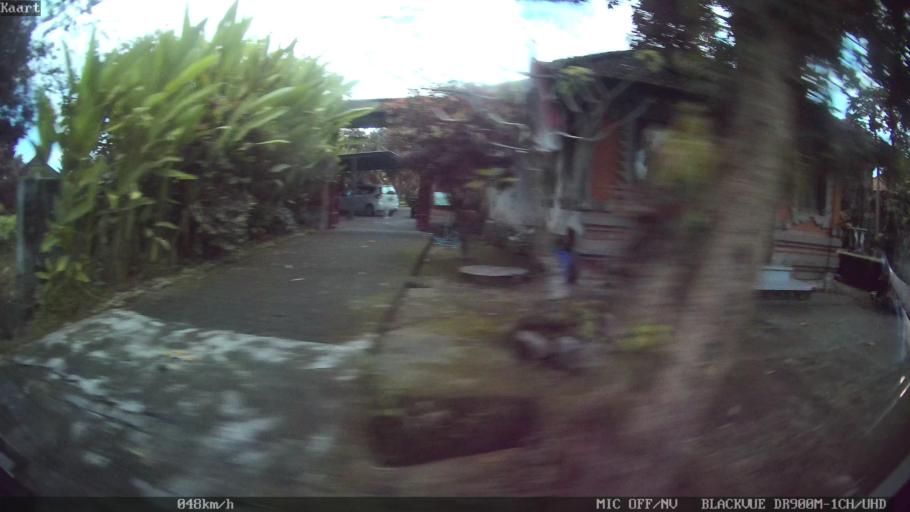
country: ID
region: Bali
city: Banjar Sedang
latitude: -8.5592
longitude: 115.2866
